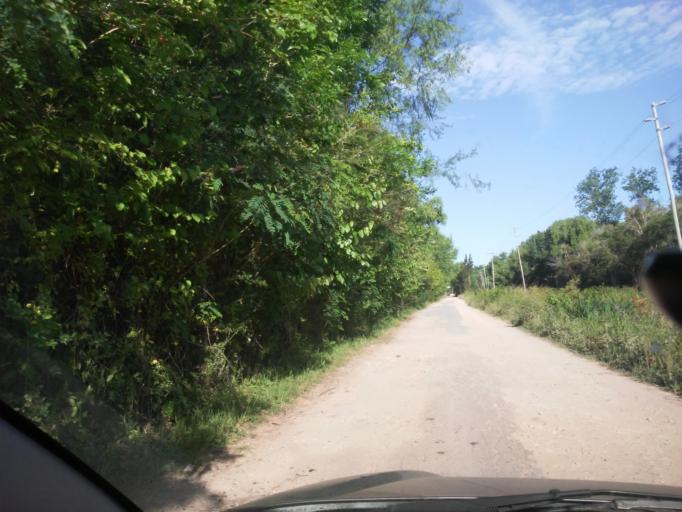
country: AR
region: Buenos Aires
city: Belen de Escobar
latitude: -34.2494
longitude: -58.7215
